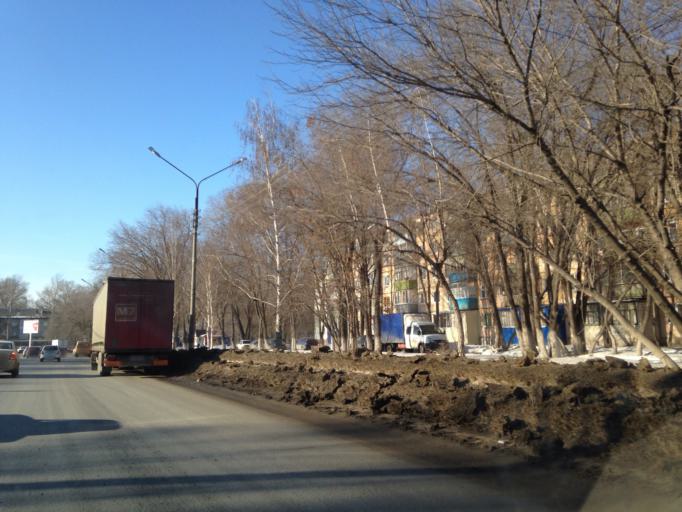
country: RU
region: Ulyanovsk
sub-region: Ulyanovskiy Rayon
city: Ulyanovsk
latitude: 54.2985
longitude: 48.3246
